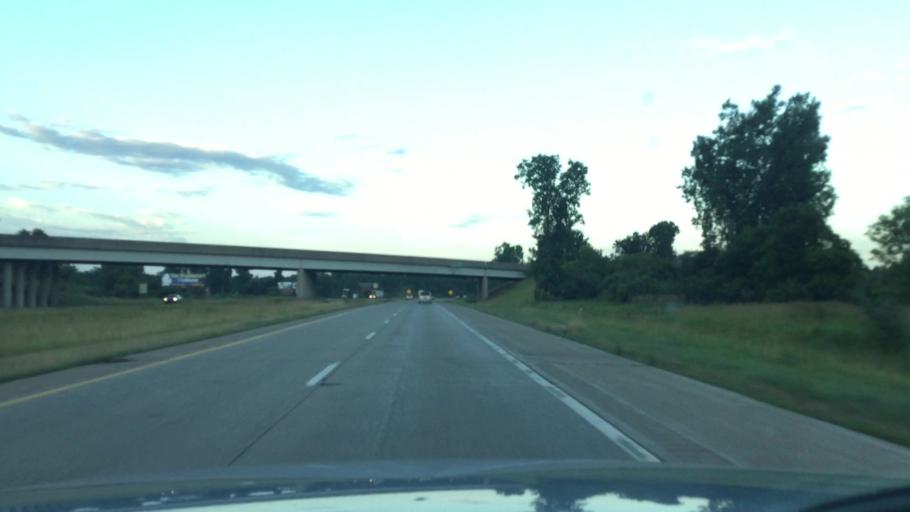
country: US
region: Michigan
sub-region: Shiawassee County
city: Perry
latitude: 42.8352
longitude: -84.2376
